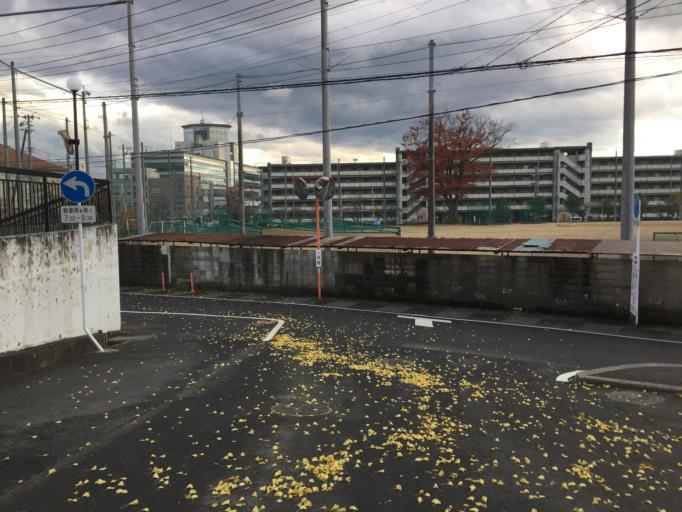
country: JP
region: Fukushima
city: Fukushima-shi
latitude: 37.7651
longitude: 140.4626
